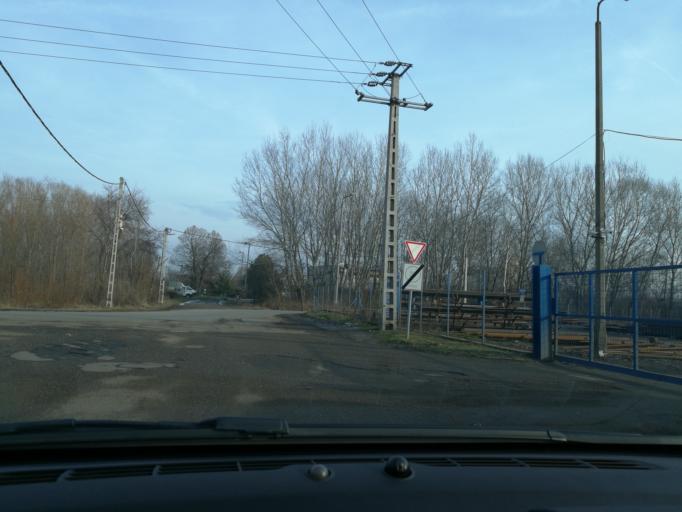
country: HU
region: Szabolcs-Szatmar-Bereg
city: Nyiregyhaza
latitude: 47.9383
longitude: 21.7074
